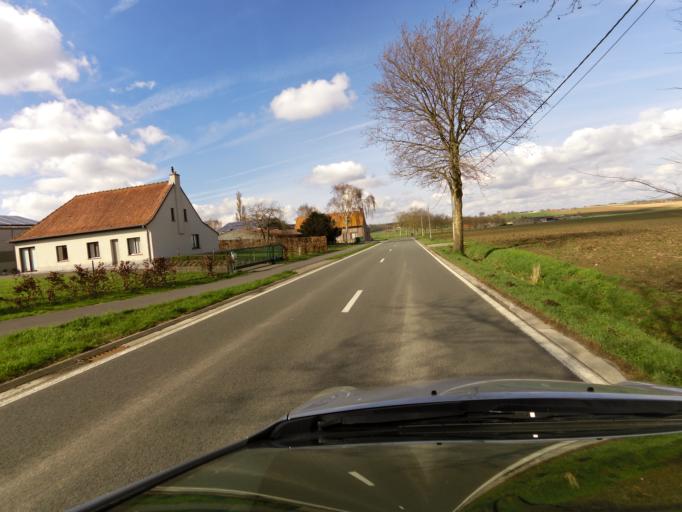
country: FR
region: Nord-Pas-de-Calais
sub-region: Departement du Nord
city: Nieppe
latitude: 50.7540
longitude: 2.8270
